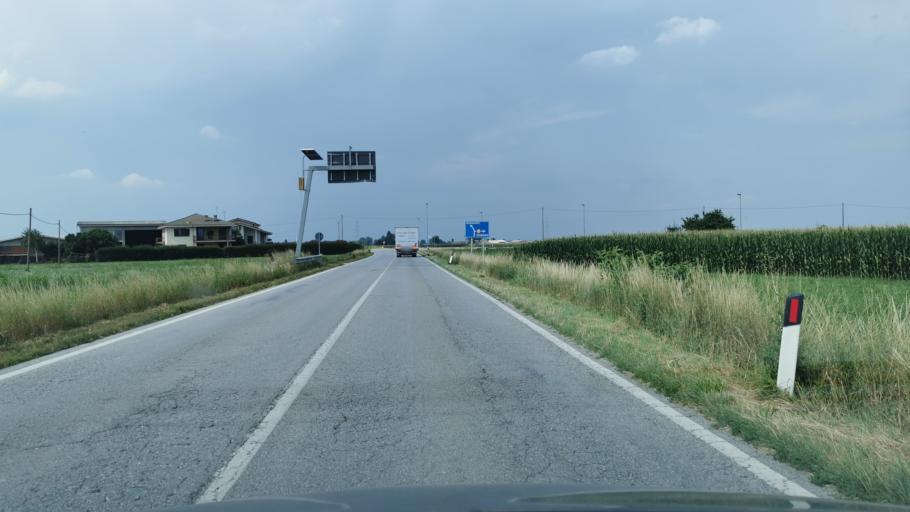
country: IT
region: Piedmont
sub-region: Provincia di Cuneo
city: Tarantasca
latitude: 44.4996
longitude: 7.5417
